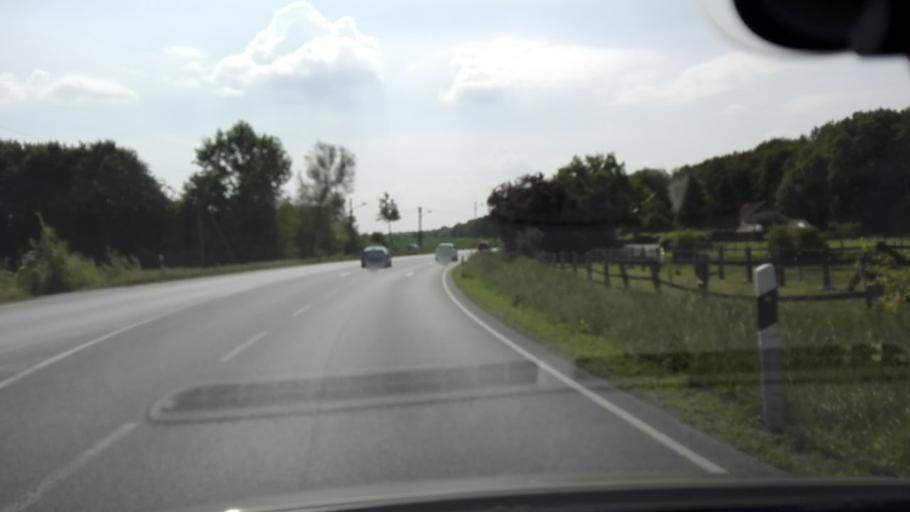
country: DE
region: North Rhine-Westphalia
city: Bergkamen
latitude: 51.6028
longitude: 7.6023
